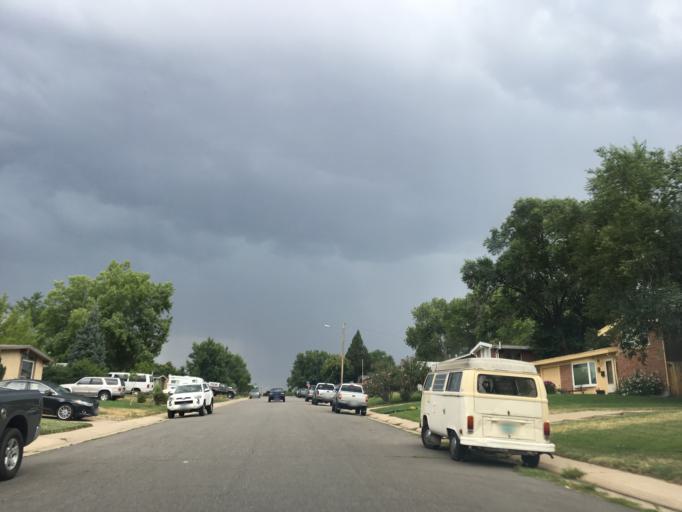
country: US
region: Colorado
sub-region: Arapahoe County
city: Sheridan
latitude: 39.6692
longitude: -105.0407
